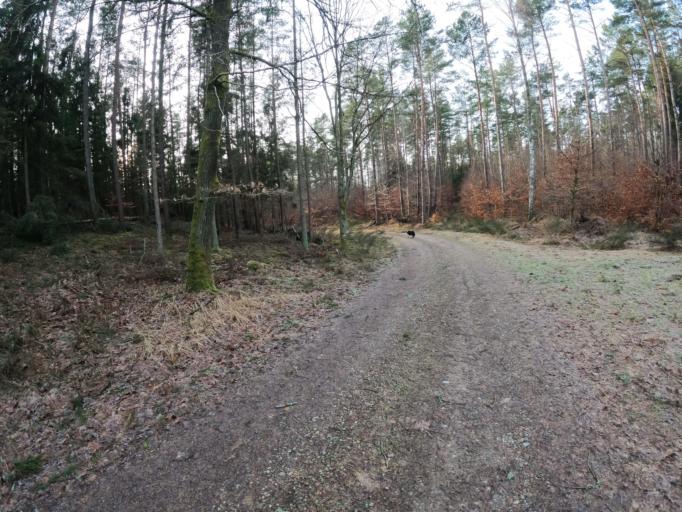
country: PL
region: West Pomeranian Voivodeship
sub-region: Powiat koszalinski
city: Polanow
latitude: 54.2060
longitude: 16.7319
